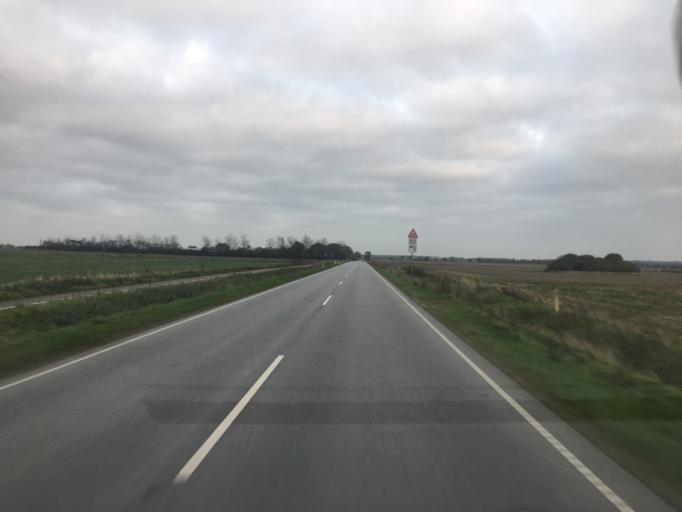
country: DE
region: Schleswig-Holstein
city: Rodenas
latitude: 54.9627
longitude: 8.7421
